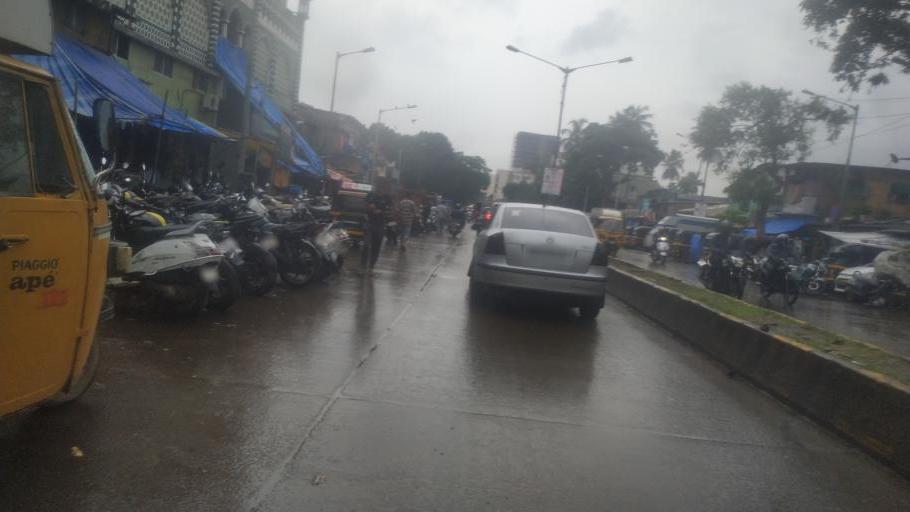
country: IN
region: Maharashtra
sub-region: Mumbai Suburban
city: Mumbai
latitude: 19.0622
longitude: 72.8732
